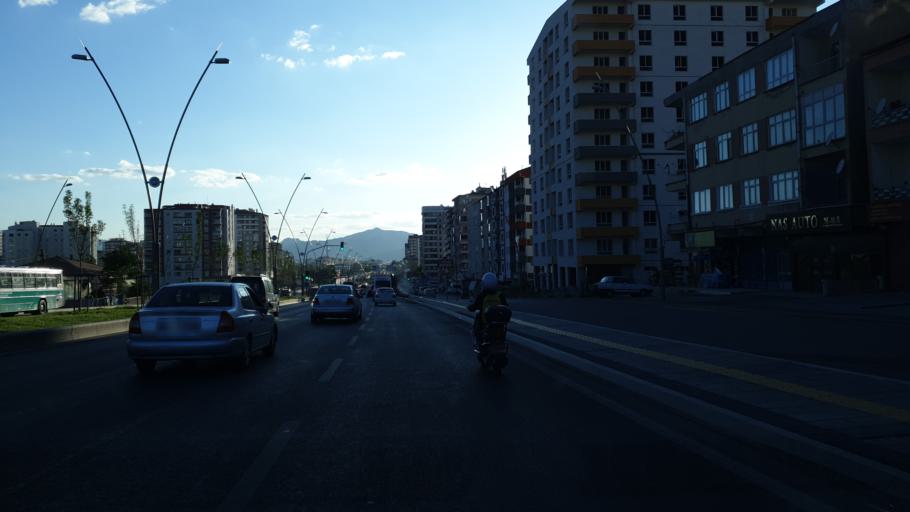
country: TR
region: Kayseri
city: Kayseri
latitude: 38.7440
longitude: 35.5256
